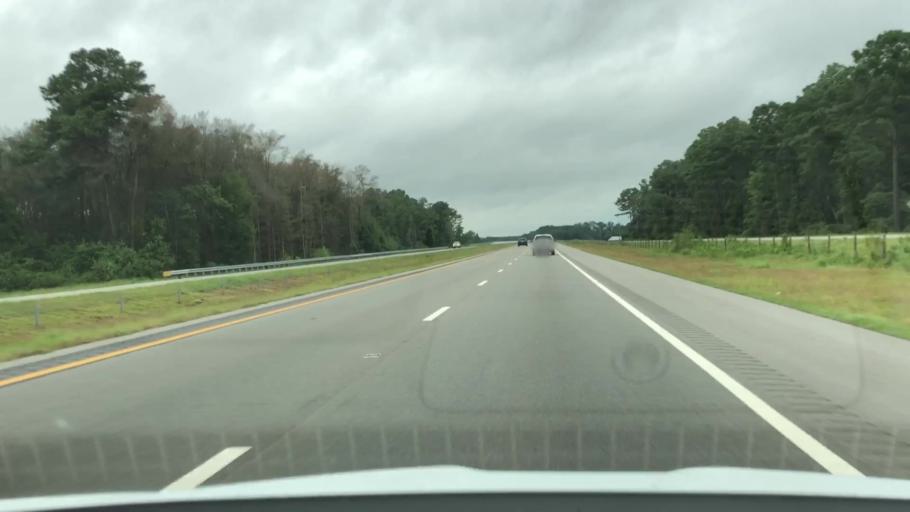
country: US
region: North Carolina
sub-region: Wayne County
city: Elroy
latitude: 35.3492
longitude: -77.8470
